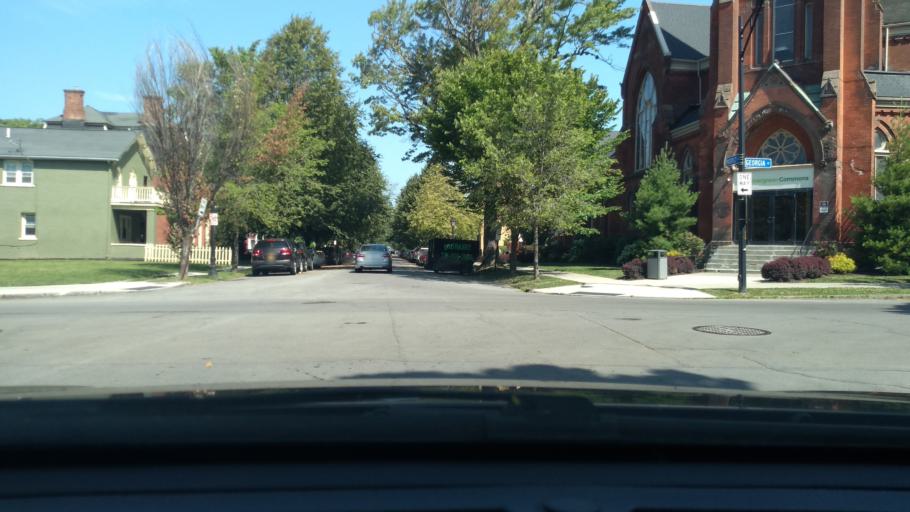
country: US
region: New York
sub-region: Erie County
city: Buffalo
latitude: 42.8908
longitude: -78.8806
